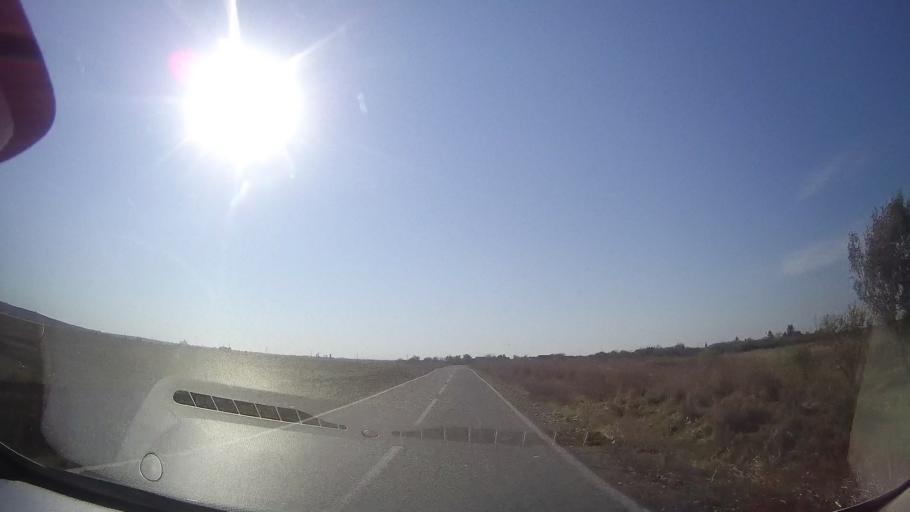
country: RO
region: Timis
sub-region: Comuna Topolovatu Mare
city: Topolovatu Mare
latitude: 45.7983
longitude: 21.5867
